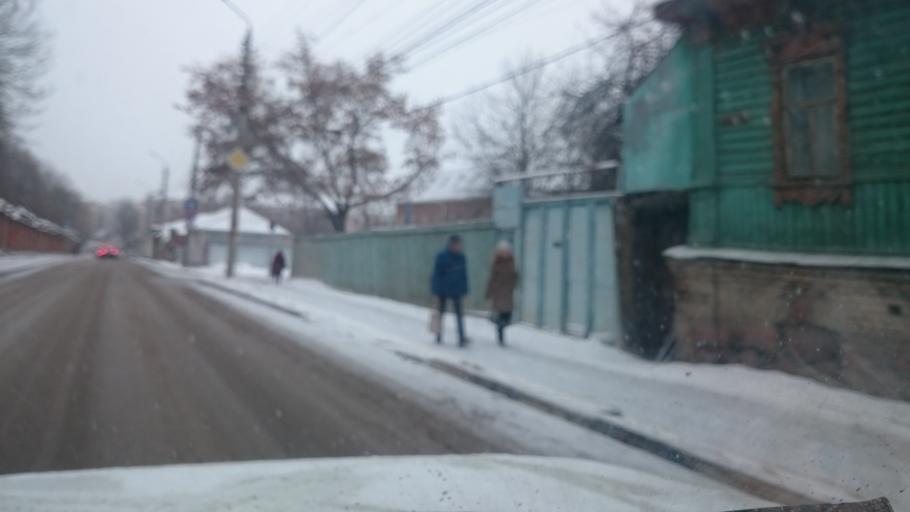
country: RU
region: Tula
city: Tula
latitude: 54.1819
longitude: 37.6119
